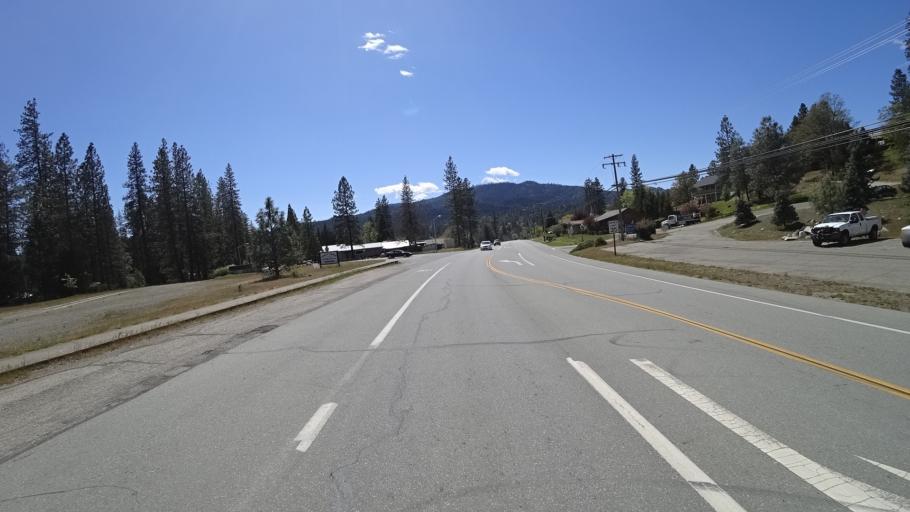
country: US
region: California
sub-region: Trinity County
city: Weaverville
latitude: 40.7347
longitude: -122.9324
